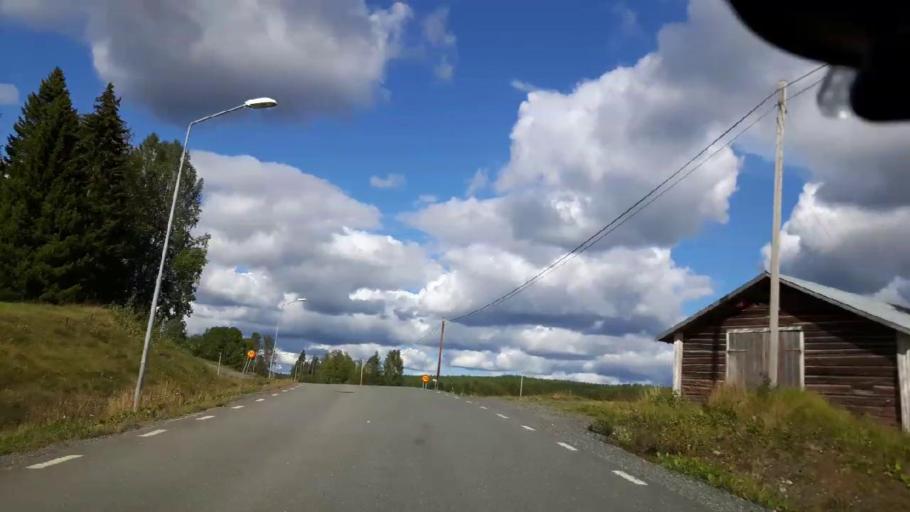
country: SE
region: Jaemtland
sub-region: Stroemsunds Kommun
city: Stroemsund
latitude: 63.3004
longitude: 15.6017
